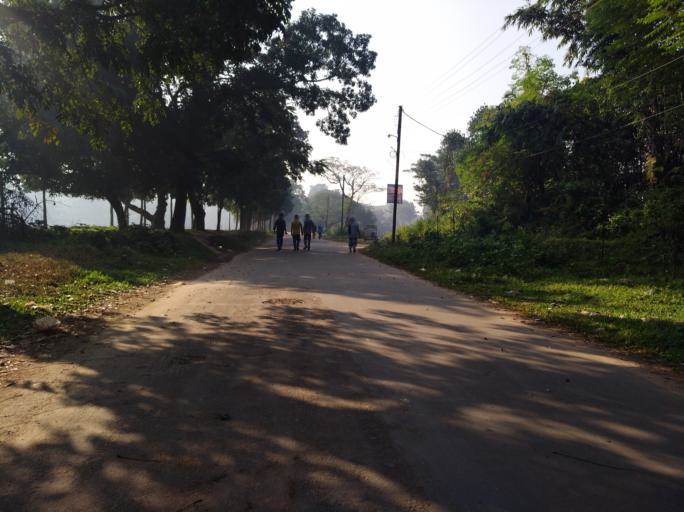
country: BD
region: Dhaka
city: Tungi
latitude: 23.8950
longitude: 90.2679
